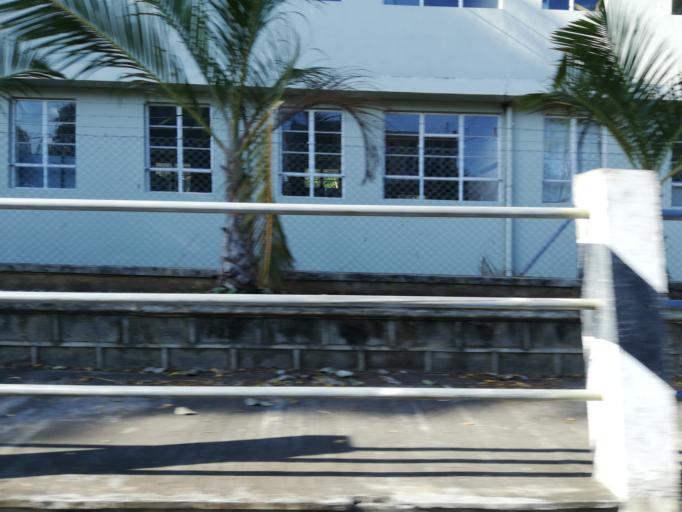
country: MU
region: Port Louis
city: Port Louis
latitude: -20.1630
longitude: 57.4888
